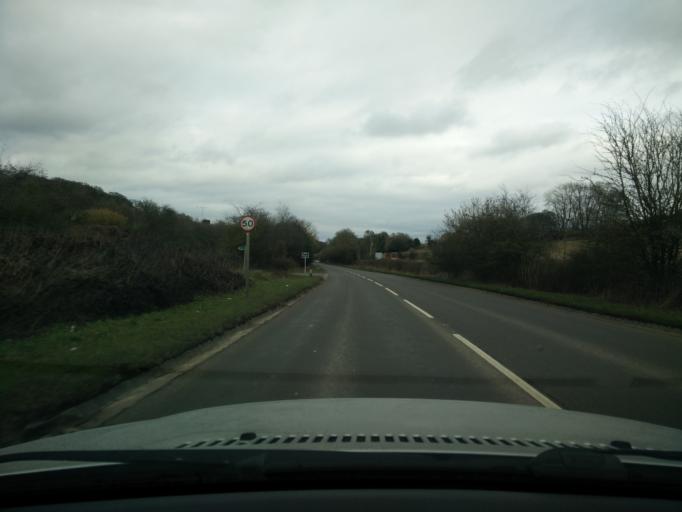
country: GB
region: England
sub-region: Buckinghamshire
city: Amersham
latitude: 51.6540
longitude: -0.6399
